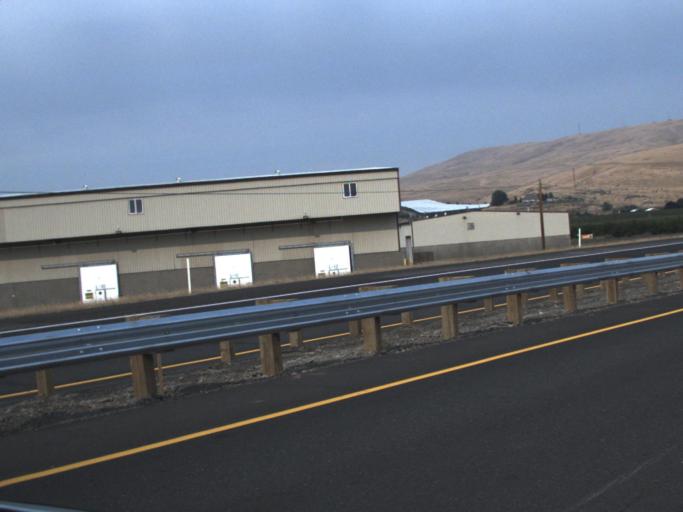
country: US
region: Washington
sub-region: Yakima County
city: Union Gap
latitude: 46.5141
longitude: -120.4770
